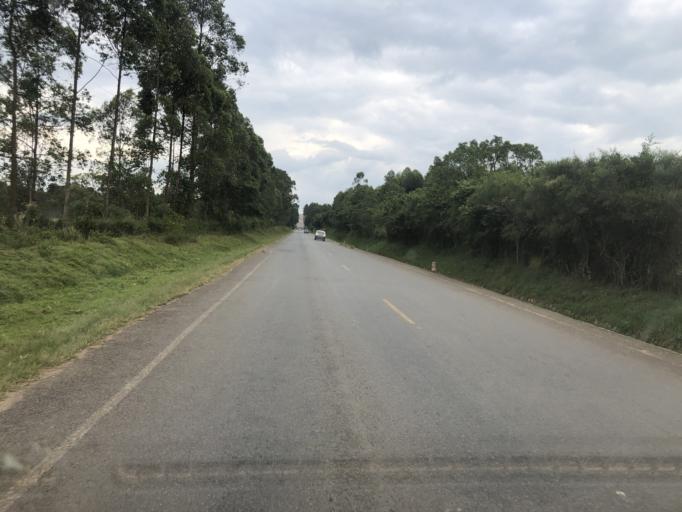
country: UG
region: Western Region
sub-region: Sheema District
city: Kibingo
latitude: -0.5791
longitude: 30.4160
